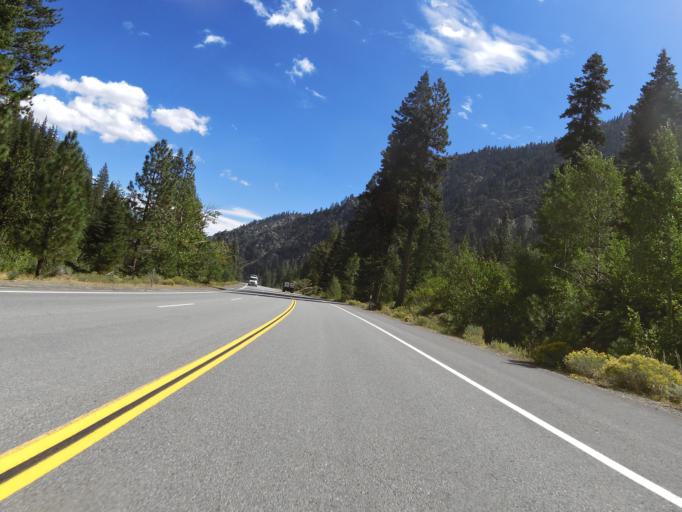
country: US
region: Nevada
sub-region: Douglas County
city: Gardnerville Ranchos
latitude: 38.7650
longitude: -119.8643
